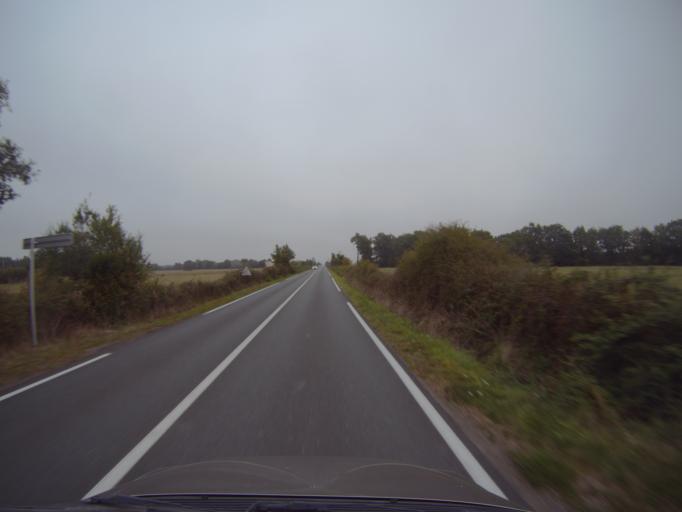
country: FR
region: Pays de la Loire
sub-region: Departement de la Vendee
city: La Bernardiere
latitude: 47.0302
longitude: -1.2627
